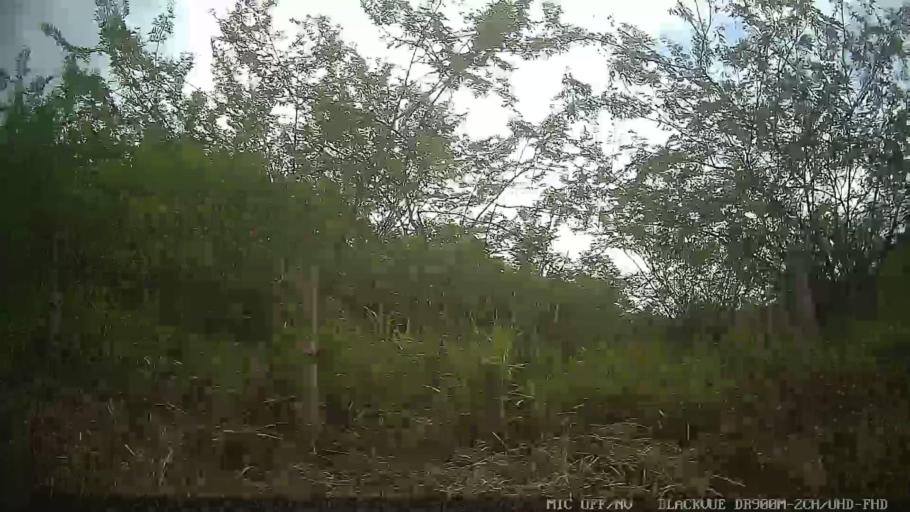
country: BR
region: Sao Paulo
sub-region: Mogi das Cruzes
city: Mogi das Cruzes
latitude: -23.4766
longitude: -46.2297
